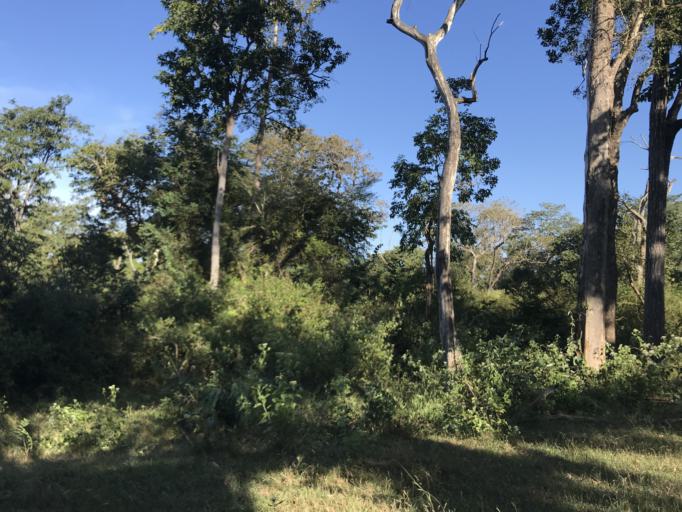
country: IN
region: Karnataka
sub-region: Mysore
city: Heggadadevankote
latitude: 11.9750
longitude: 76.2413
